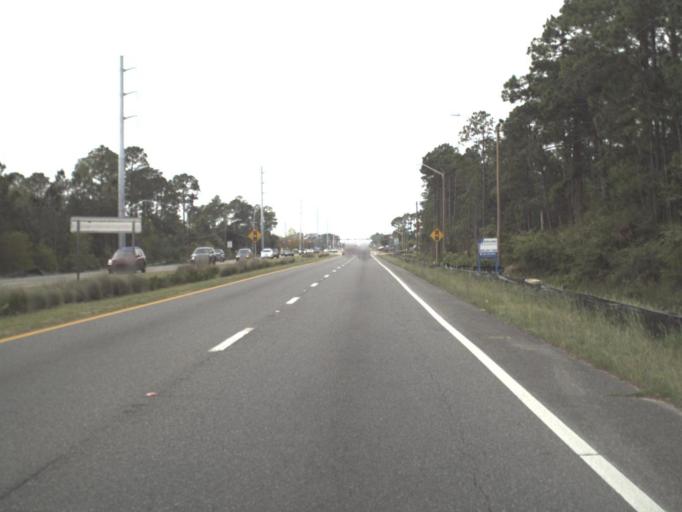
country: US
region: Florida
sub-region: Santa Rosa County
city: Tiger Point
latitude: 30.3912
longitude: -87.0583
